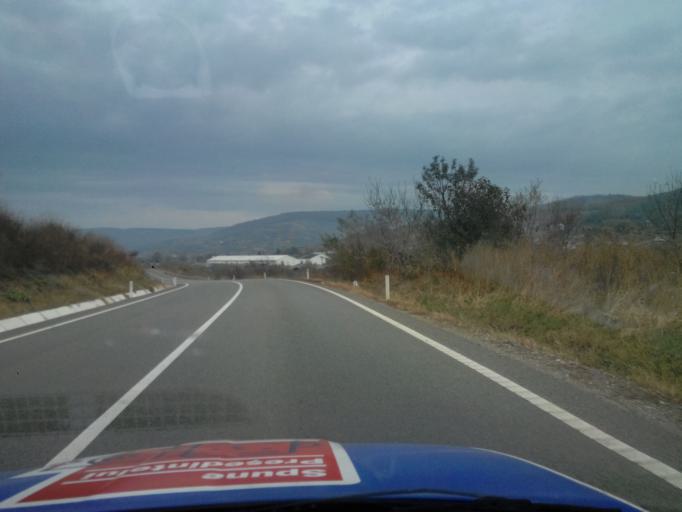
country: RO
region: Vaslui
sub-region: Comuna Tatarani
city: Tatarani
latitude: 46.6363
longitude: 27.9566
